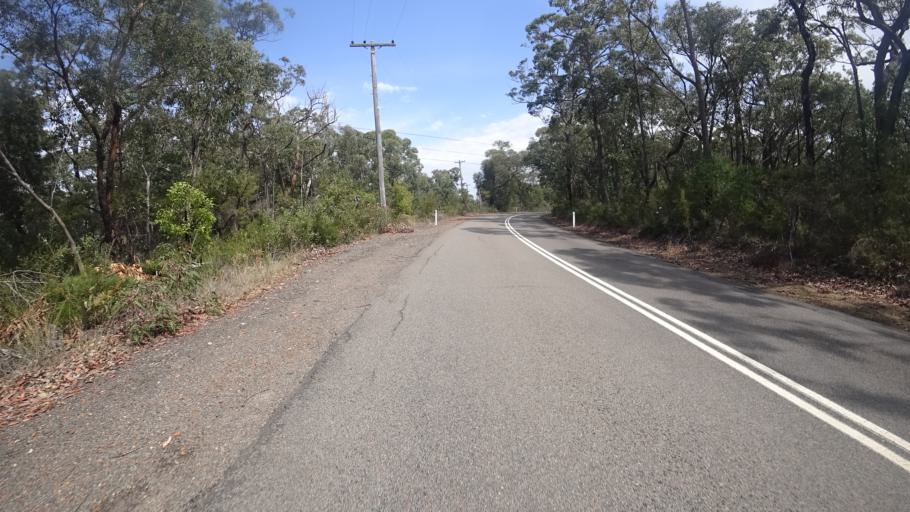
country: AU
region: New South Wales
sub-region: Hornsby Shire
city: Mount Colah
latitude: -33.6754
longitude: 151.1370
